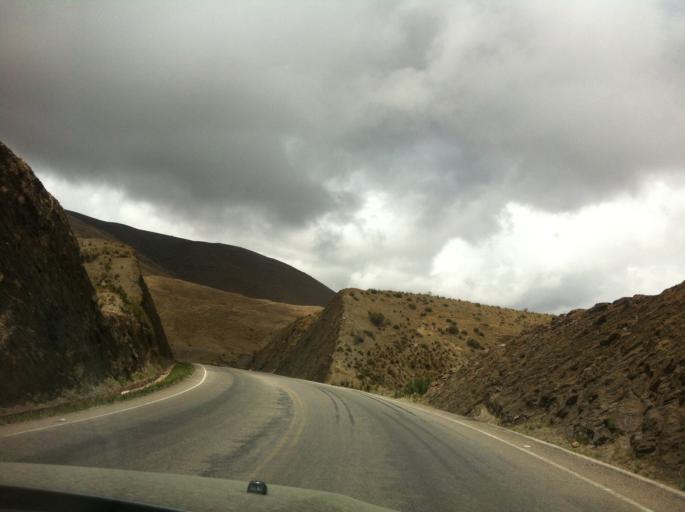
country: BO
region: Cochabamba
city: Irpa Irpa
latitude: -17.7087
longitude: -66.5292
